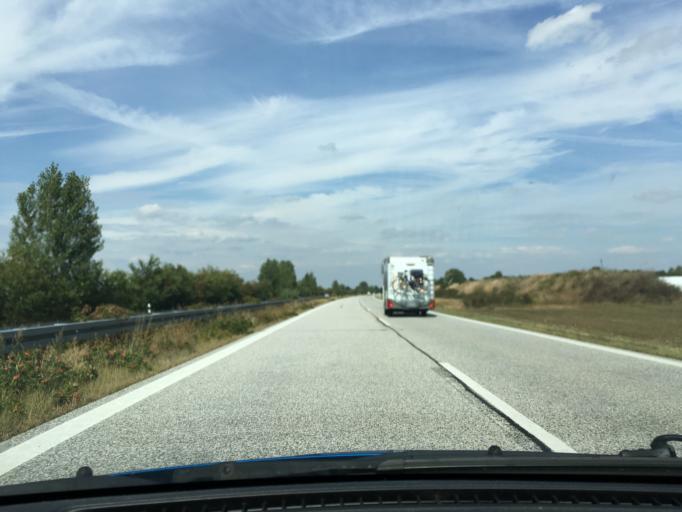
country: DE
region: Mecklenburg-Vorpommern
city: Mirow
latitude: 53.4606
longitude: 11.4948
